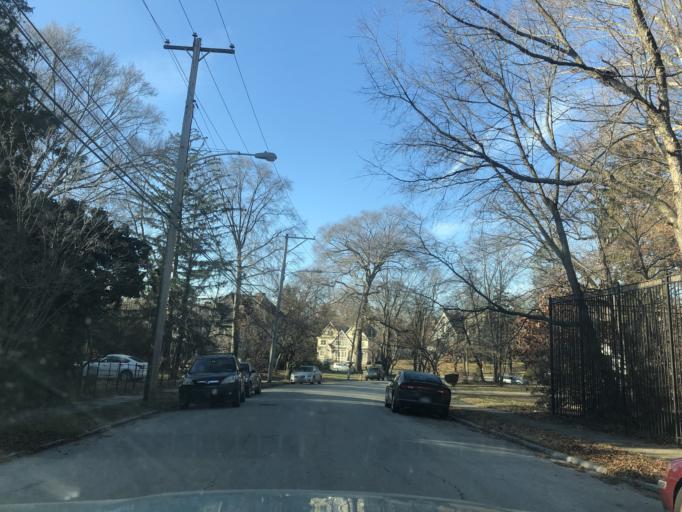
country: US
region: Pennsylvania
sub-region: Montgomery County
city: Bala-Cynwyd
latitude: 39.9898
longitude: -75.2448
